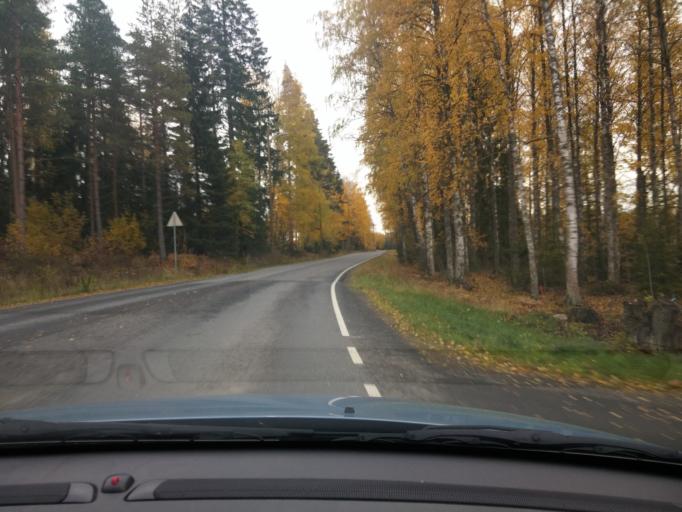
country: FI
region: Haeme
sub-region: Forssa
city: Tammela
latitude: 60.8020
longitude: 23.8112
